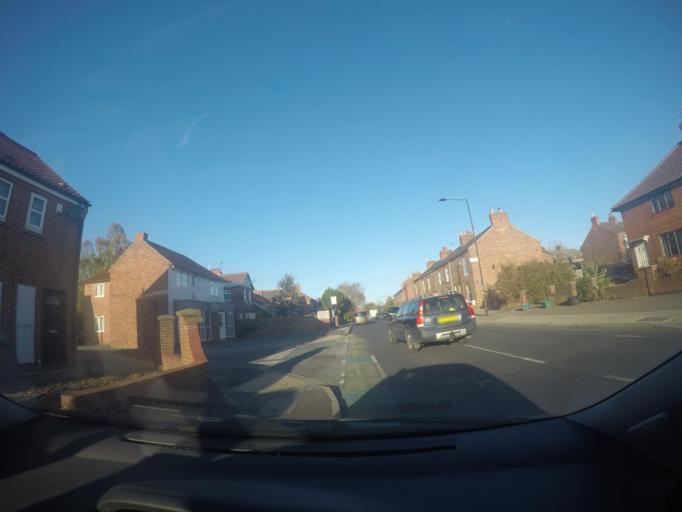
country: GB
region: England
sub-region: City of York
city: York
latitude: 53.9791
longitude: -1.0698
